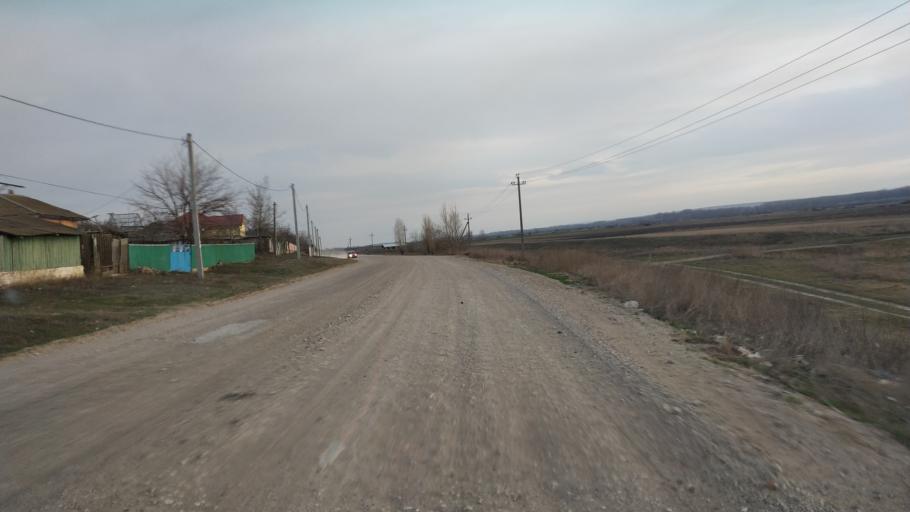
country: MD
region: Hincesti
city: Dancu
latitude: 46.7763
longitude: 28.1968
